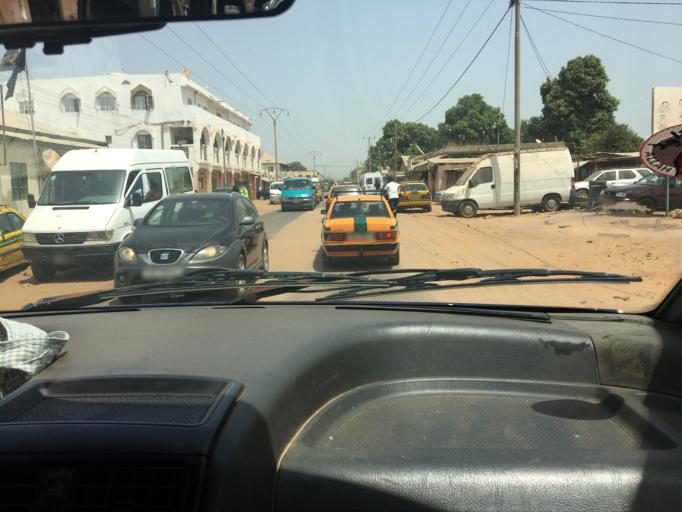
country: GM
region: Western
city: Abuko
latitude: 13.3982
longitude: -16.6733
